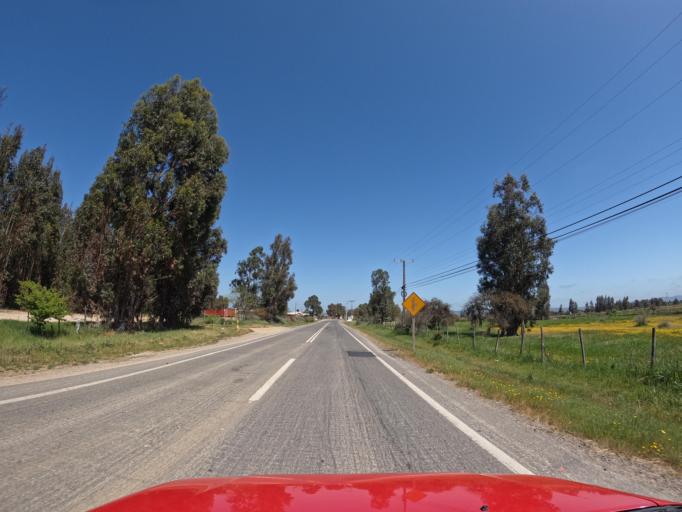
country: CL
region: O'Higgins
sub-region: Provincia de Colchagua
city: Santa Cruz
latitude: -34.7326
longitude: -71.6837
